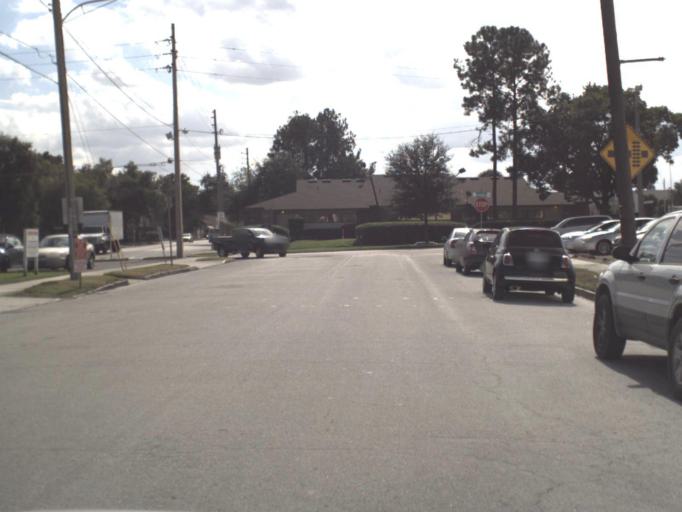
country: US
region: Florida
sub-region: Orange County
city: Orlando
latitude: 28.5284
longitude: -81.3818
